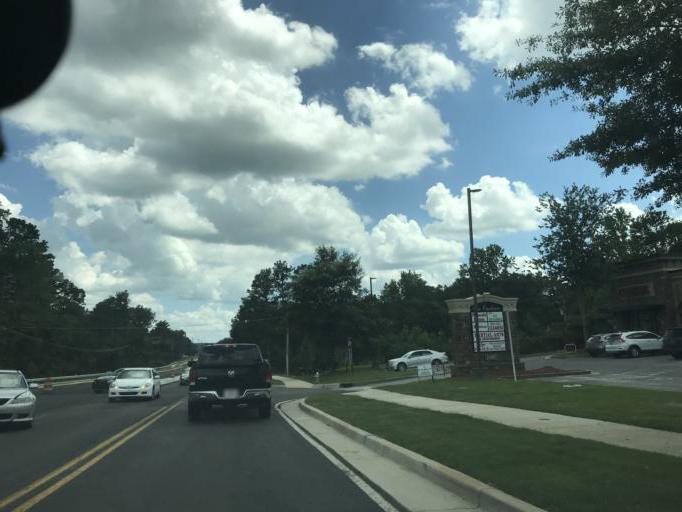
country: US
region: Georgia
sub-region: Forsyth County
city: Cumming
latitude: 34.2380
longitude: -84.1948
